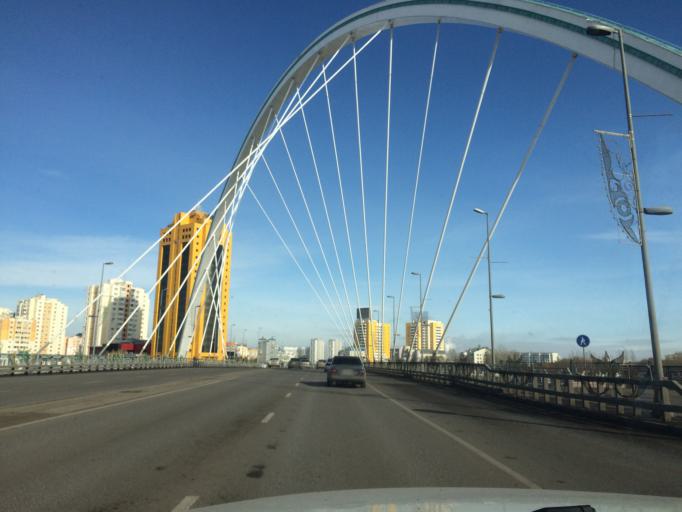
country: KZ
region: Astana Qalasy
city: Astana
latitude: 51.1511
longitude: 71.4272
